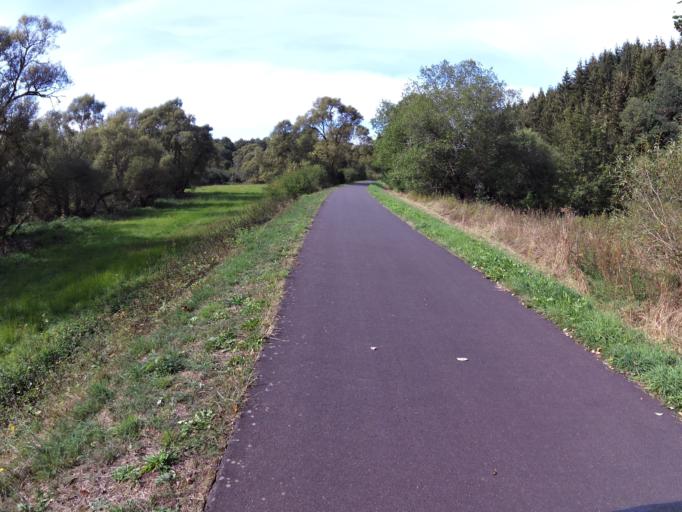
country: DE
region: Rheinland-Pfalz
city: Pronsfeld
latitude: 50.1629
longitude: 6.3196
